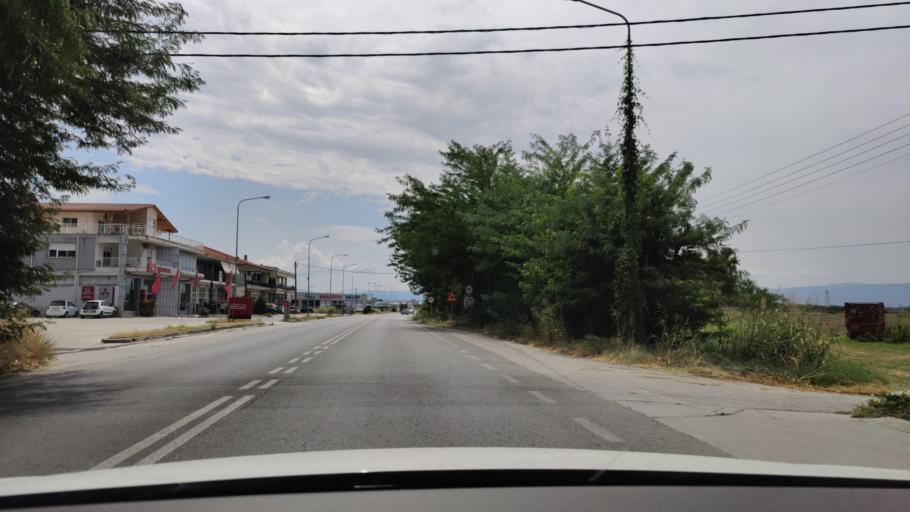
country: GR
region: Central Macedonia
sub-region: Nomos Serron
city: Serres
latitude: 41.0698
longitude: 23.5405
